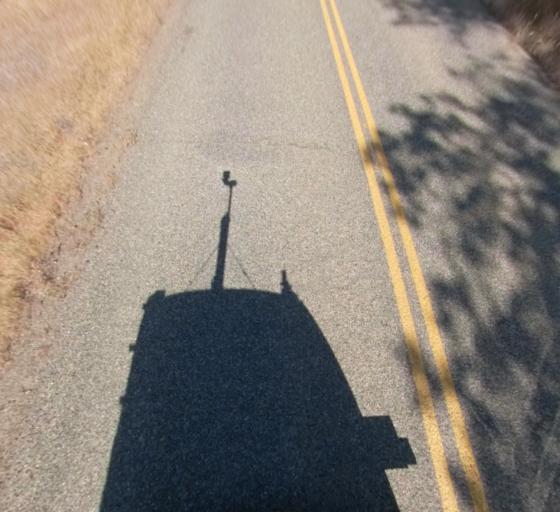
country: US
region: California
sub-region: Fresno County
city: Auberry
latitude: 37.2161
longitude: -119.3555
